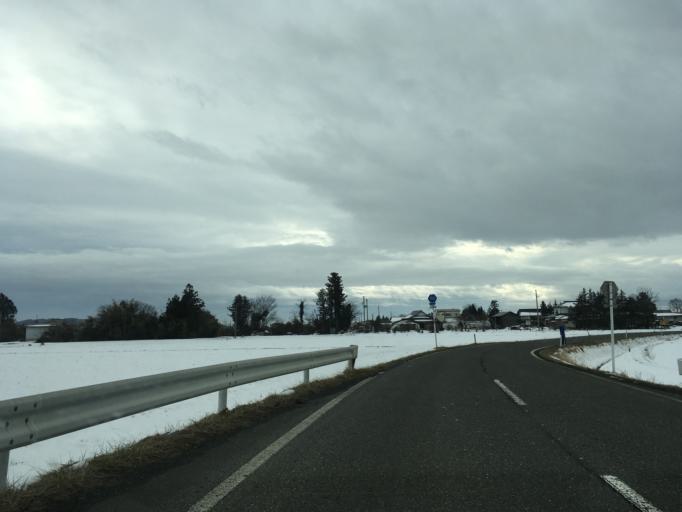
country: JP
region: Iwate
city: Ichinoseki
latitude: 38.7825
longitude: 141.1527
